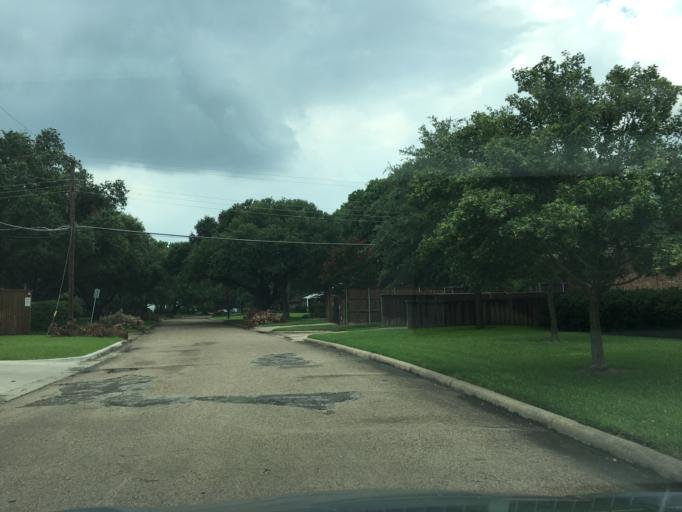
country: US
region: Texas
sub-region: Dallas County
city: Addison
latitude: 32.9109
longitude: -96.8074
